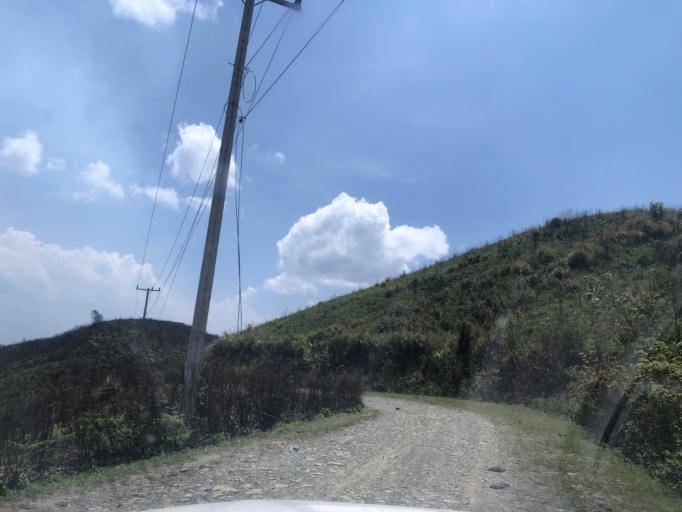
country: LA
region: Phongsali
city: Phongsali
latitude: 21.4119
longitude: 102.1881
